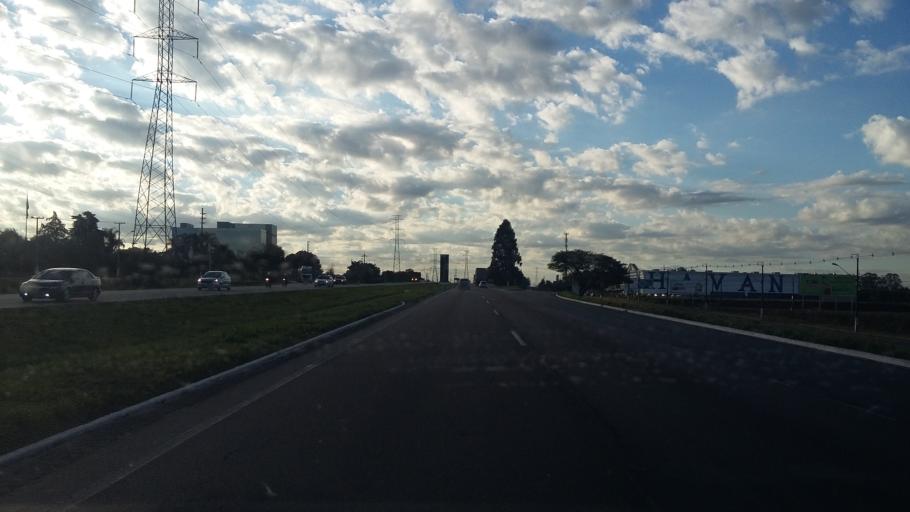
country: BR
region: Parana
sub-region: Curitiba
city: Curitiba
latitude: -25.4563
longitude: -49.3606
